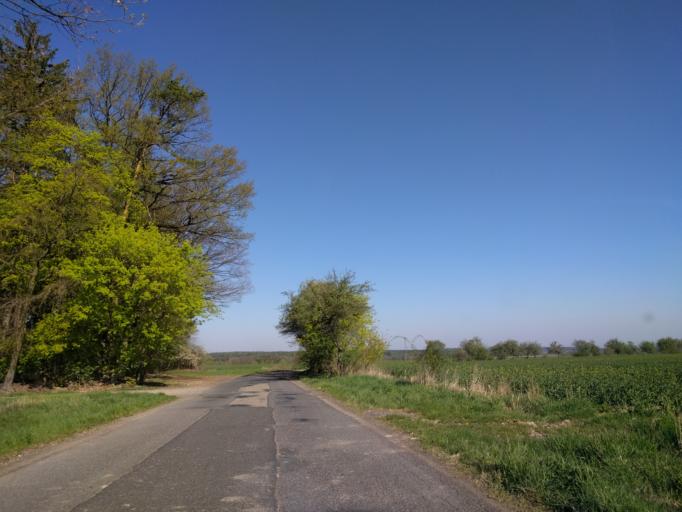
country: CZ
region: Central Bohemia
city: Mukarov
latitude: 49.9950
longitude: 14.7744
